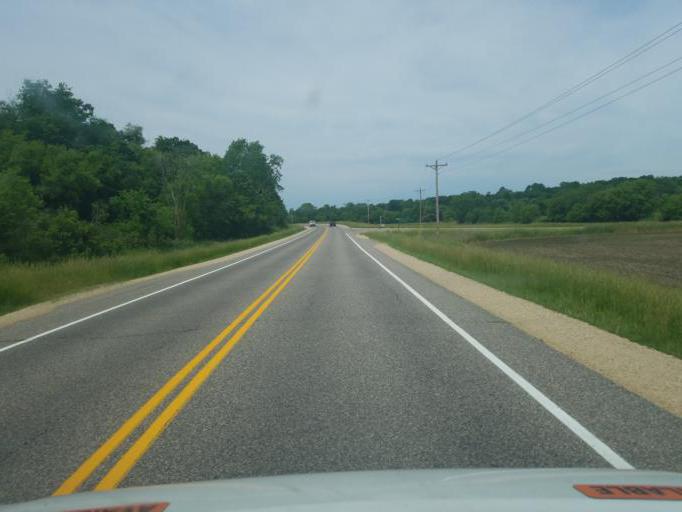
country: US
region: Wisconsin
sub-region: Juneau County
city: Elroy
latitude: 43.7657
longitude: -90.2478
